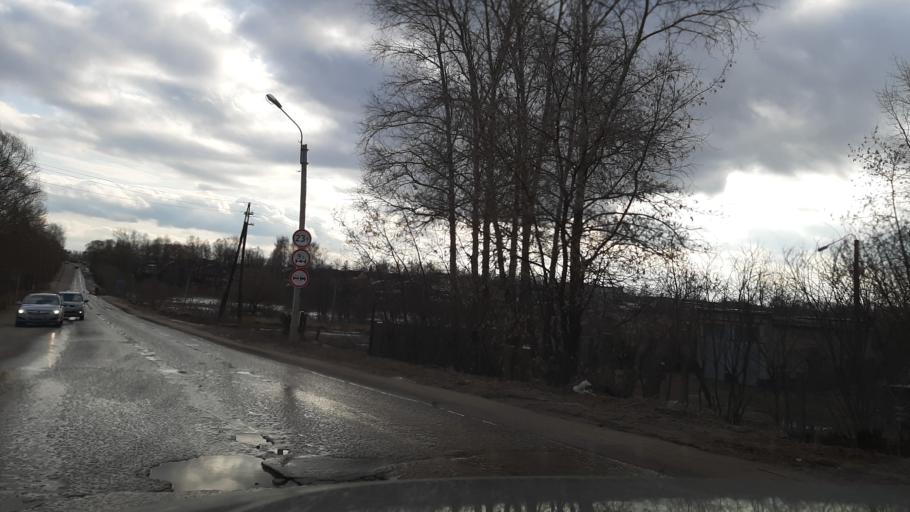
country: RU
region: Ivanovo
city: Teykovo
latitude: 56.8591
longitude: 40.5199
